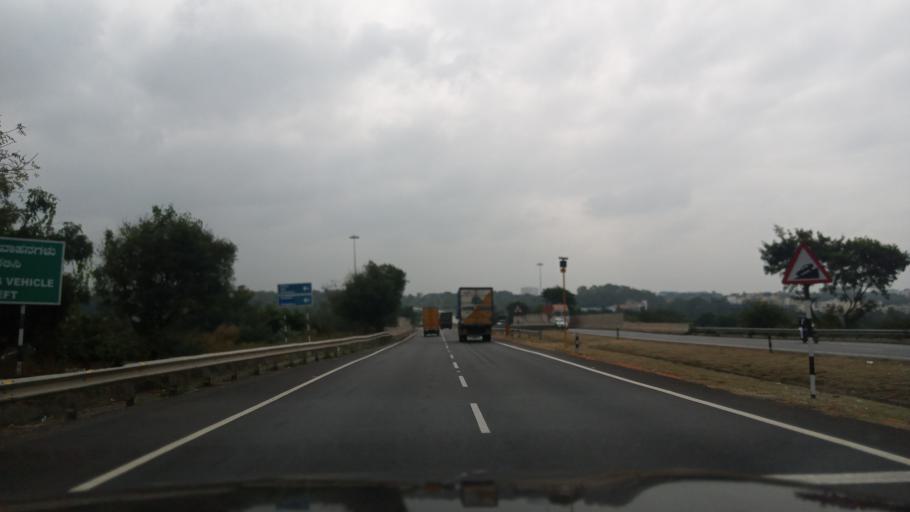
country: IN
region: Karnataka
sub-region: Bangalore Urban
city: Bangalore
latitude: 12.9078
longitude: 77.4686
